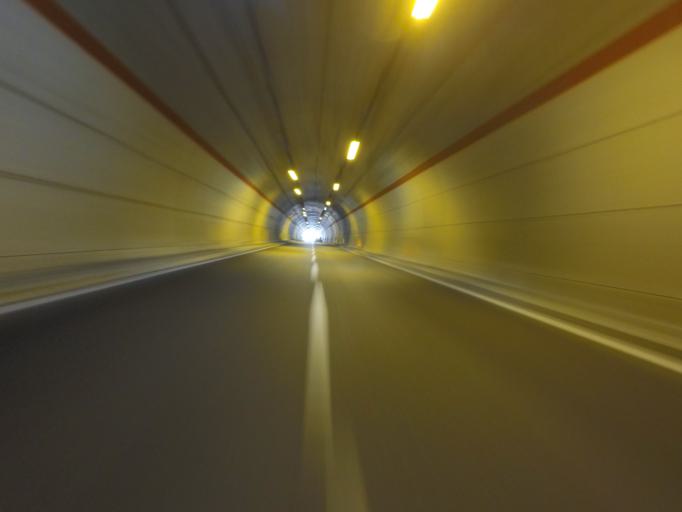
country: IT
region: Tuscany
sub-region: Provincia di Siena
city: Rosia
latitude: 43.2441
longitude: 11.2870
